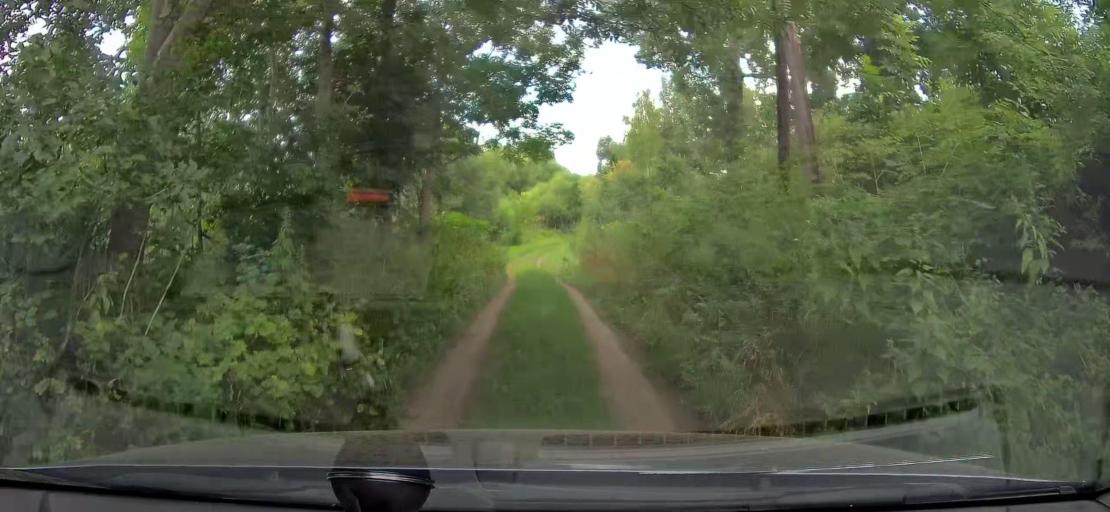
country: RU
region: Kursk
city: Zolotukhino
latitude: 52.0307
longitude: 36.1987
